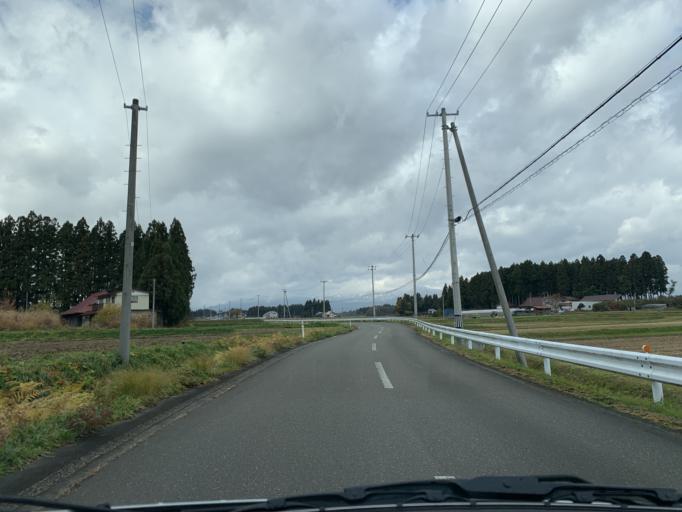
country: JP
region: Iwate
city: Mizusawa
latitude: 39.0735
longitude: 141.0585
